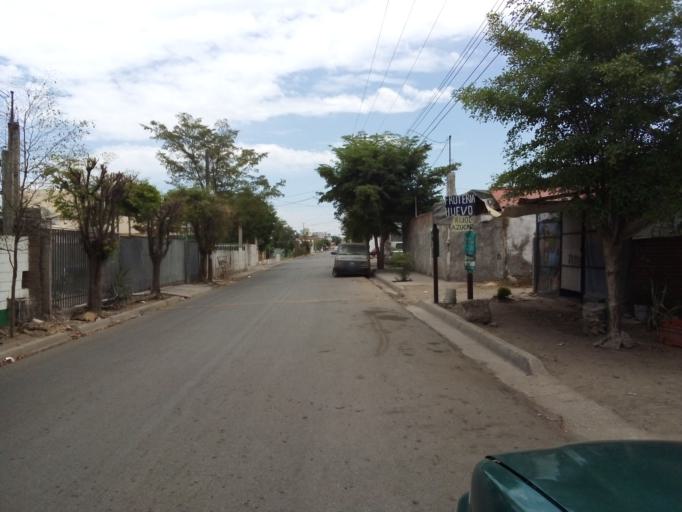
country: MX
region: Sinaloa
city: Culiacan
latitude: 24.7714
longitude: -107.4310
